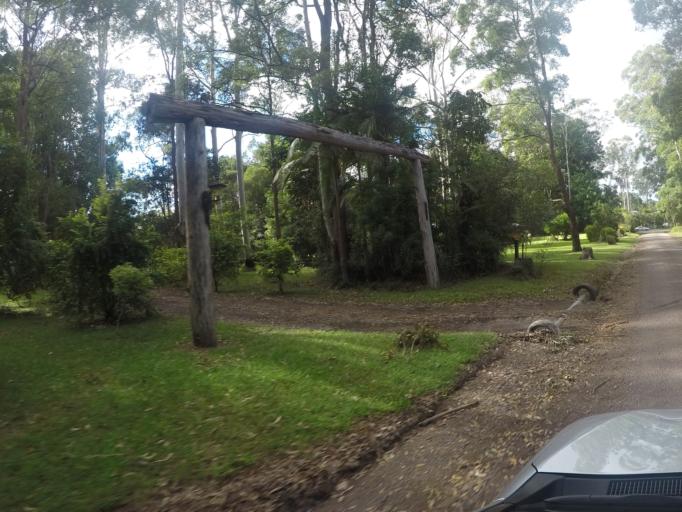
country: AU
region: Queensland
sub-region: Sunshine Coast
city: Nambour
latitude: -26.6187
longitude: 152.8613
